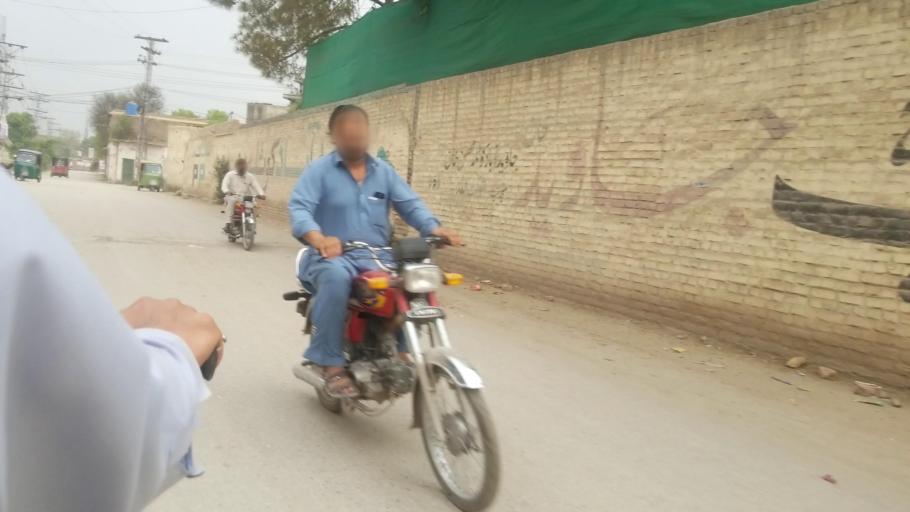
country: PK
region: Khyber Pakhtunkhwa
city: Peshawar
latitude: 33.9863
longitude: 71.5533
